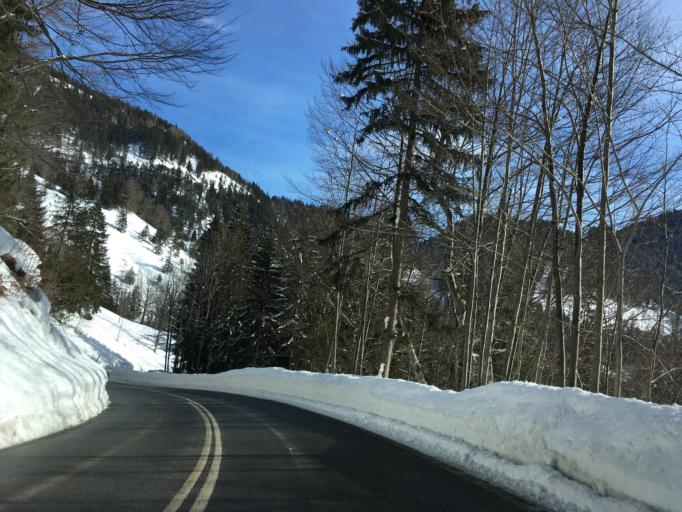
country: DE
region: Bavaria
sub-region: Upper Bavaria
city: Bayrischzell
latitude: 47.6785
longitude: 12.0153
